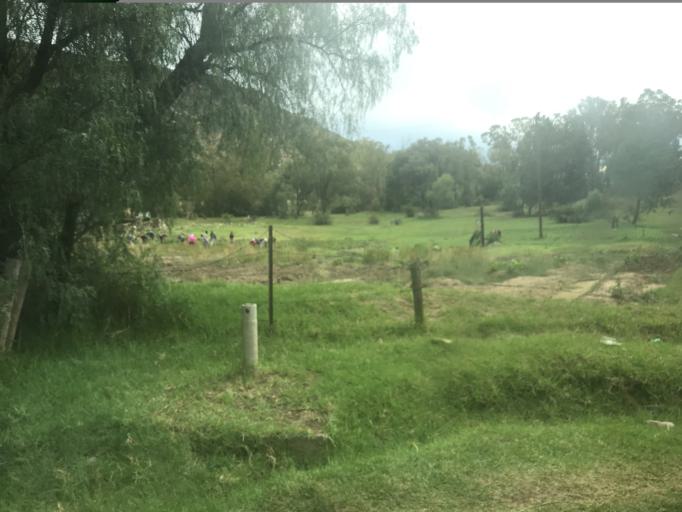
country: LS
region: Maseru
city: Nako
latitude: -29.6311
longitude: 27.5037
